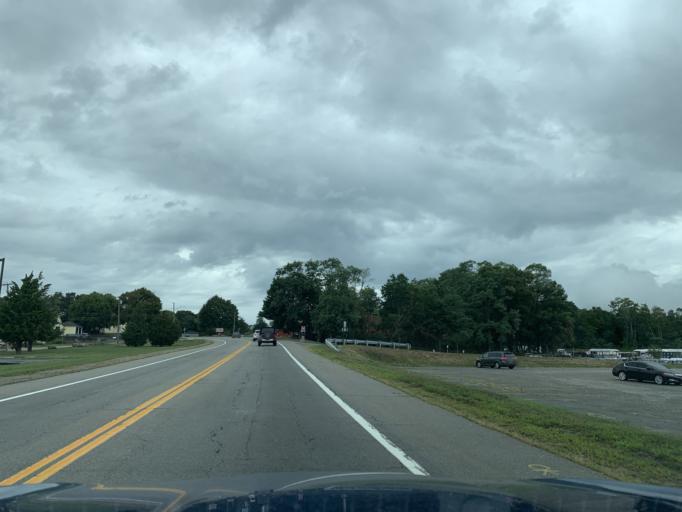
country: US
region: Rhode Island
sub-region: Bristol County
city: Warren
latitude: 41.7495
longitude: -71.2716
